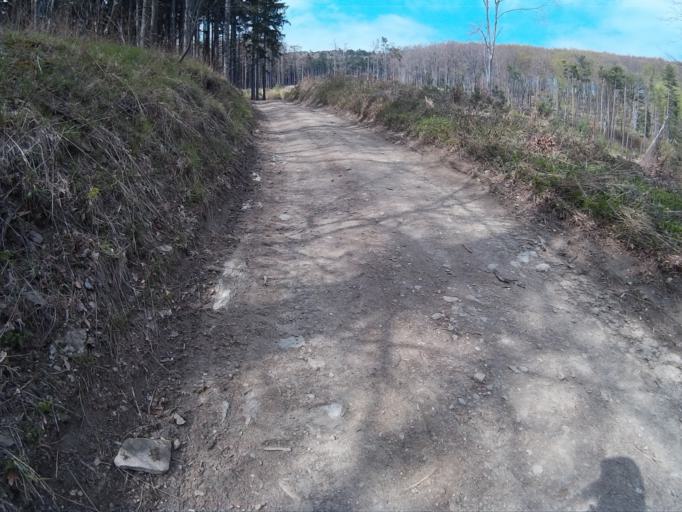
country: AT
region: Burgenland
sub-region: Politischer Bezirk Oberwart
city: Rechnitz
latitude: 47.3498
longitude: 16.4461
